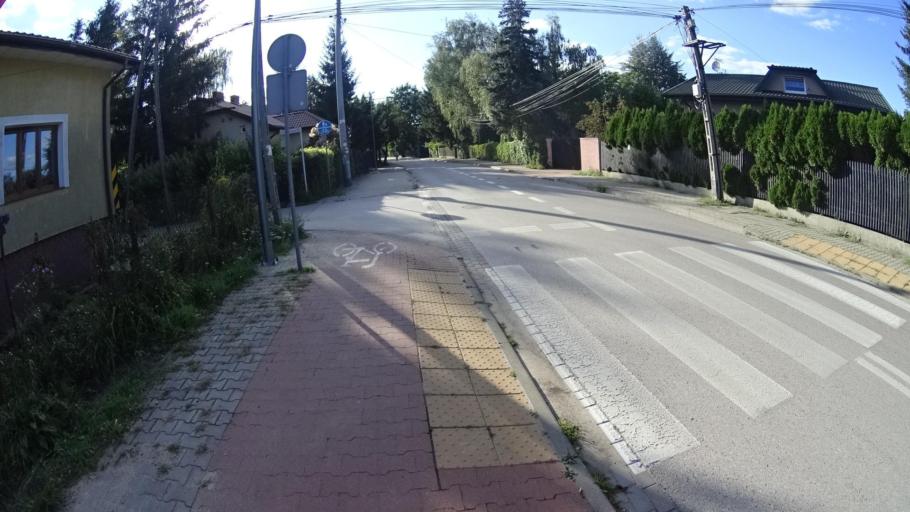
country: PL
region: Masovian Voivodeship
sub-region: Powiat piaseczynski
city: Piaseczno
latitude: 52.0658
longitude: 20.9933
